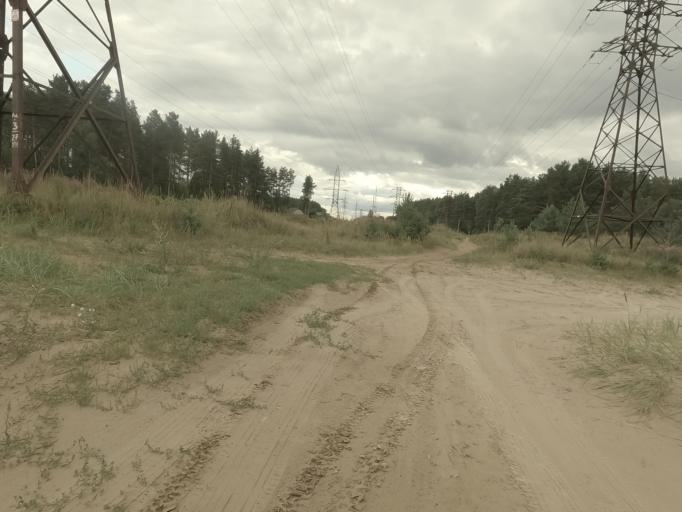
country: RU
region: Leningrad
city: Kirovsk
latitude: 59.8985
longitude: 31.0041
